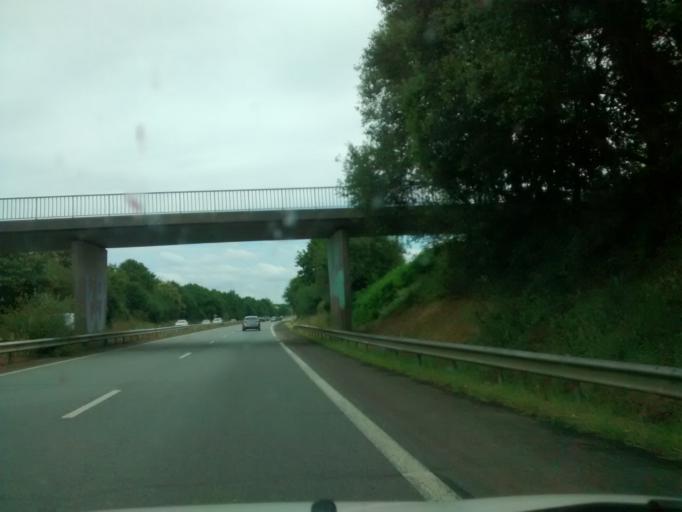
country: FR
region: Brittany
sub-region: Departement des Cotes-d'Armor
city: Caulnes
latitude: 48.2822
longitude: -2.1943
